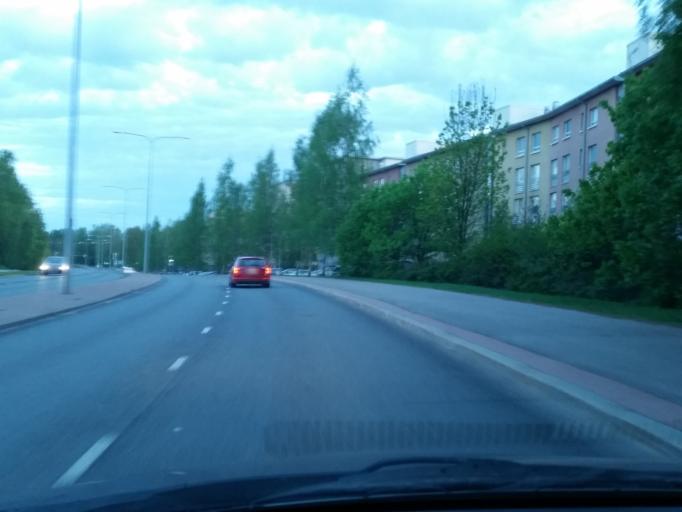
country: FI
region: Uusimaa
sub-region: Helsinki
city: Vantaa
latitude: 60.1910
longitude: 25.0396
